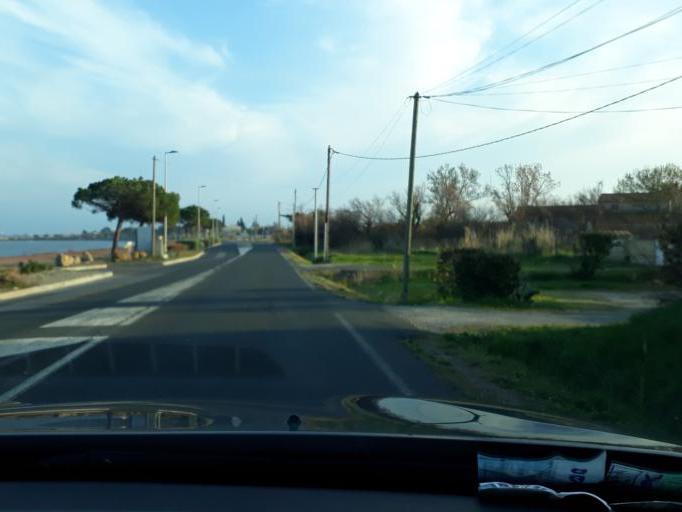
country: FR
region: Languedoc-Roussillon
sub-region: Departement de l'Herault
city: Marseillan
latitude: 43.3443
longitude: 3.5317
